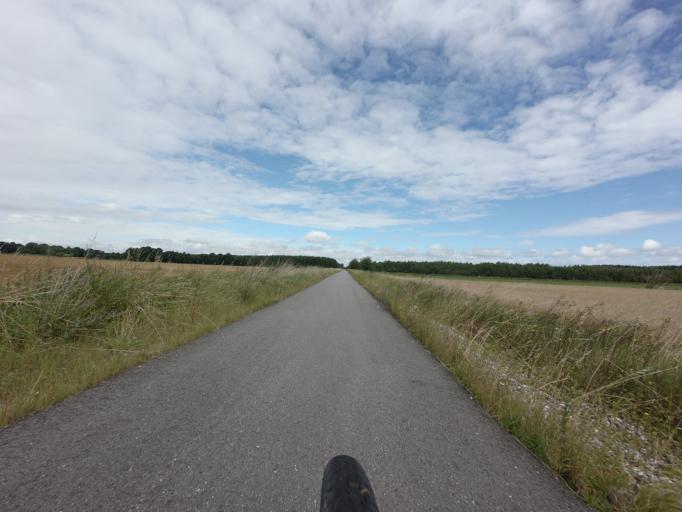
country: DK
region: Central Jutland
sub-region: Norddjurs Kommune
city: Auning
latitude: 56.4115
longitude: 10.3933
